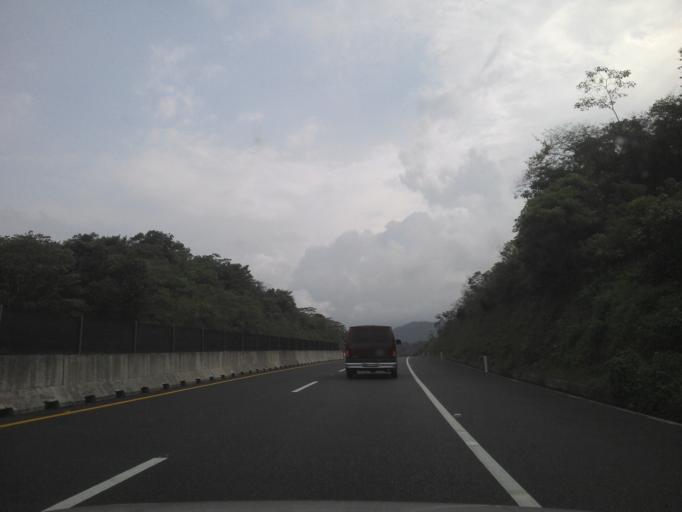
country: MX
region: Puebla
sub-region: Xicotepec
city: San Lorenzo
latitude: 20.4096
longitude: -97.9360
